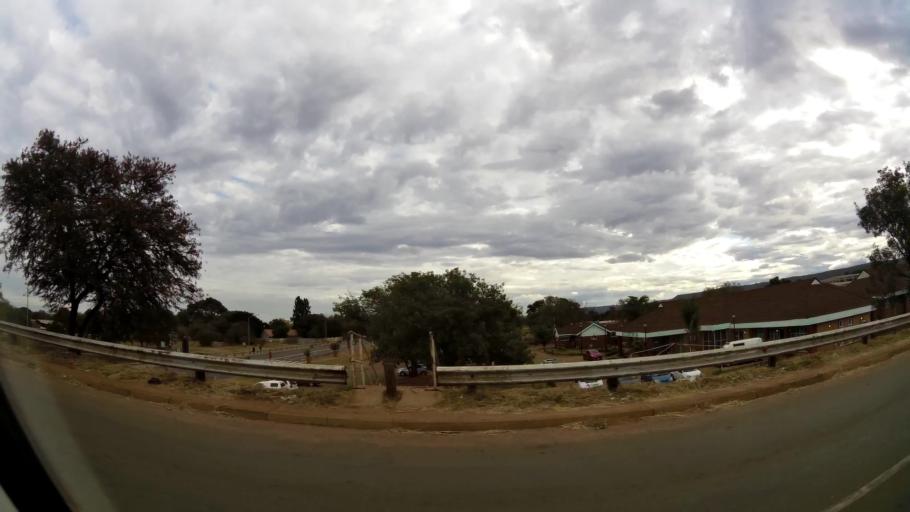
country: ZA
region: Limpopo
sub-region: Waterberg District Municipality
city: Modimolle
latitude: -24.5243
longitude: 28.7090
